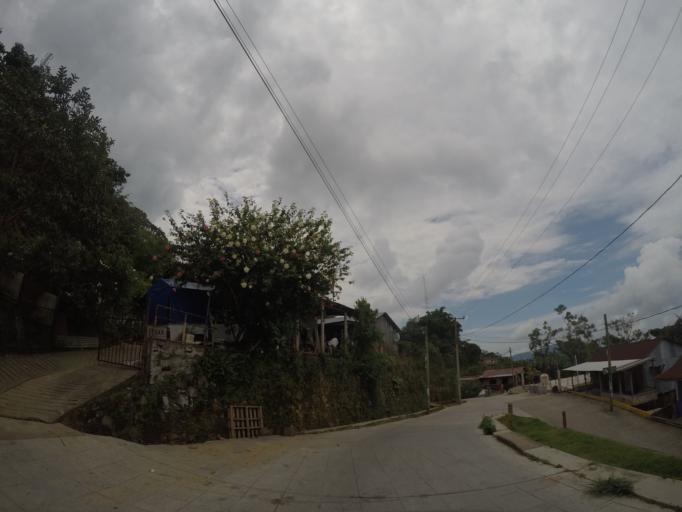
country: MX
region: Oaxaca
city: Pluma Hidalgo
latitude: 15.9246
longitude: -96.4187
